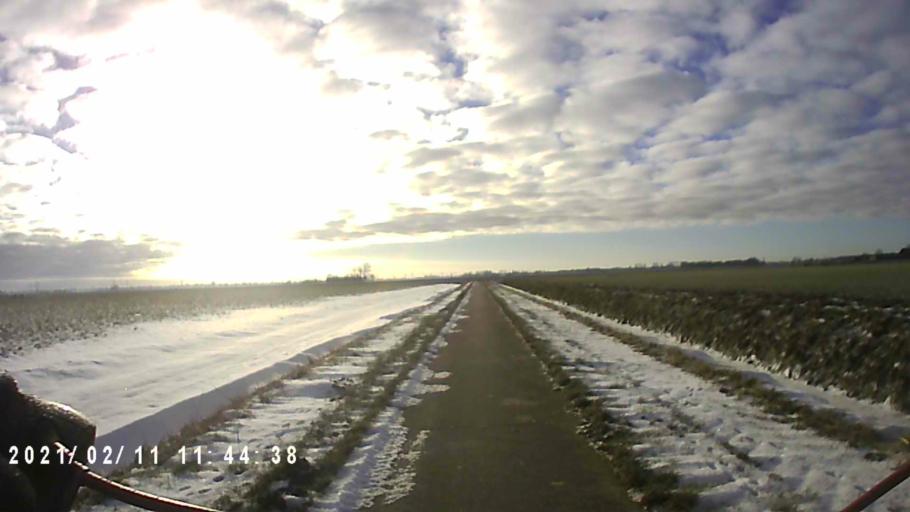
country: NL
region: Groningen
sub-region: Gemeente Zuidhorn
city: Aduard
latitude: 53.2837
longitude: 6.4534
